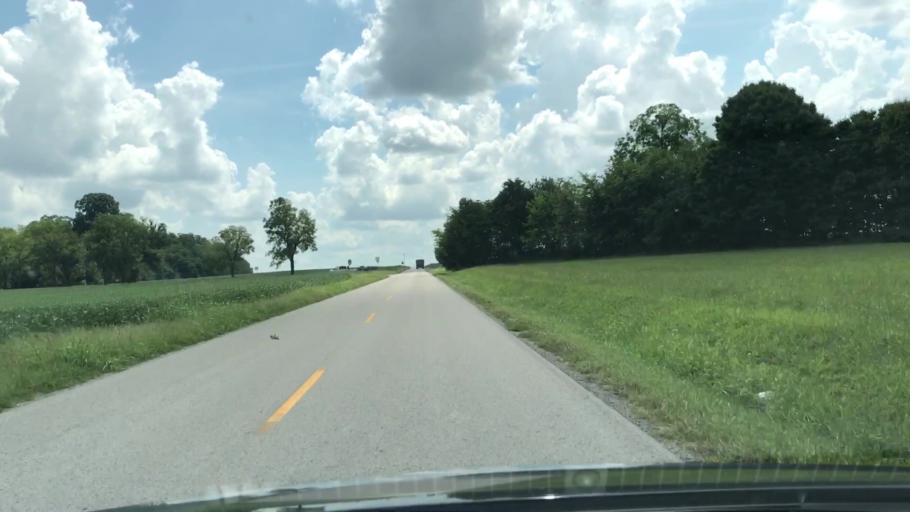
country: US
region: Kentucky
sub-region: Todd County
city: Guthrie
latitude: 36.7012
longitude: -87.0413
